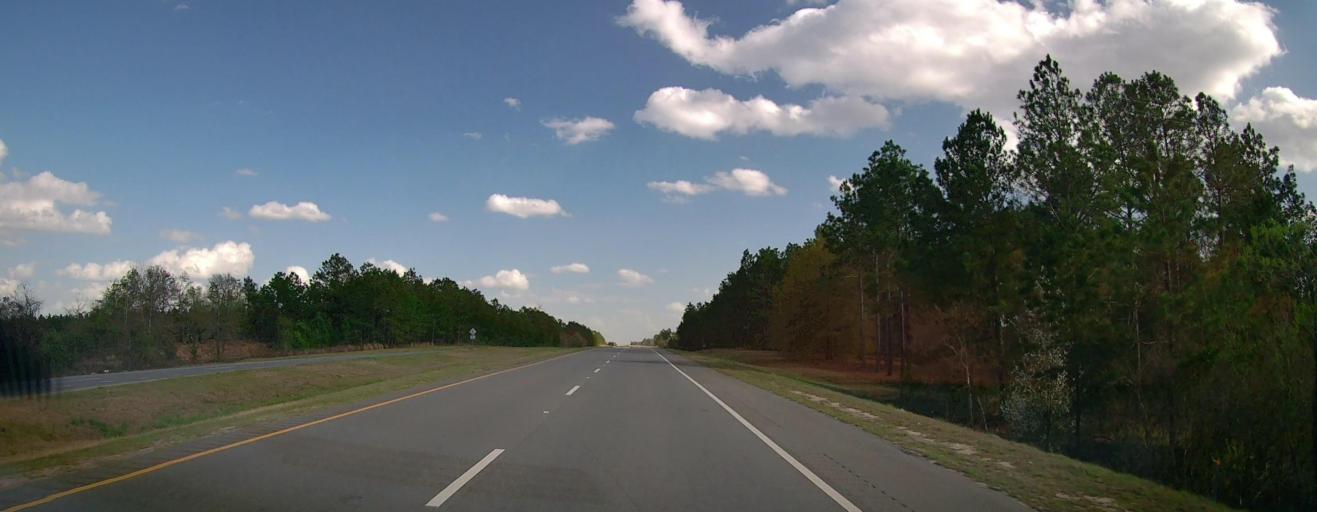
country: US
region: Georgia
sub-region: Telfair County
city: Helena
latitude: 32.0908
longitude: -82.9403
